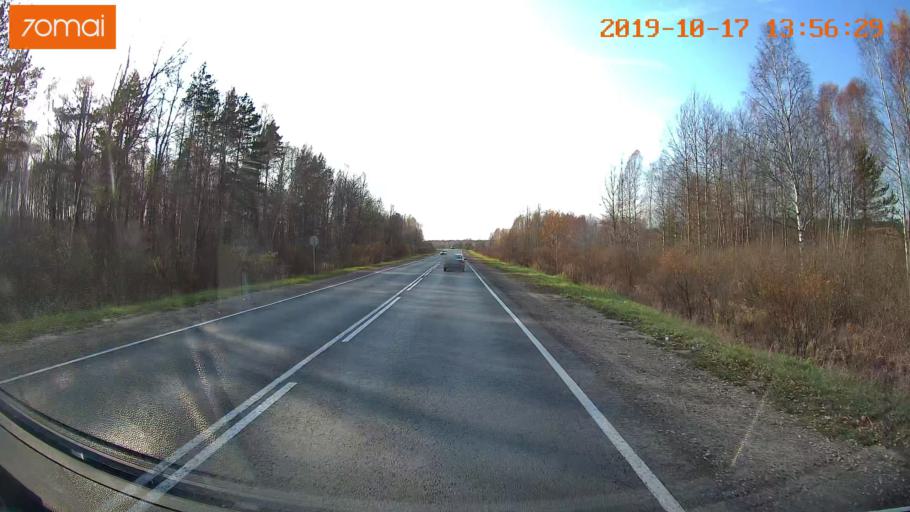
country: RU
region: Rjazan
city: Spas-Klepiki
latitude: 55.1508
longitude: 40.2655
